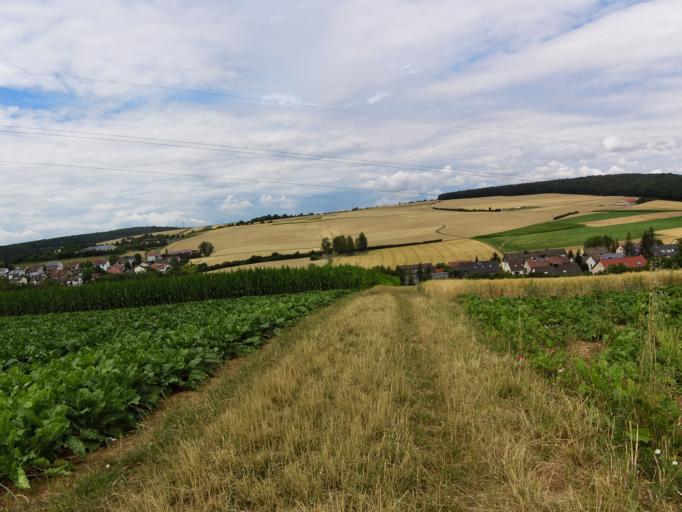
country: DE
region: Bavaria
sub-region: Regierungsbezirk Unterfranken
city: Estenfeld
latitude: 49.8221
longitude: 9.9760
